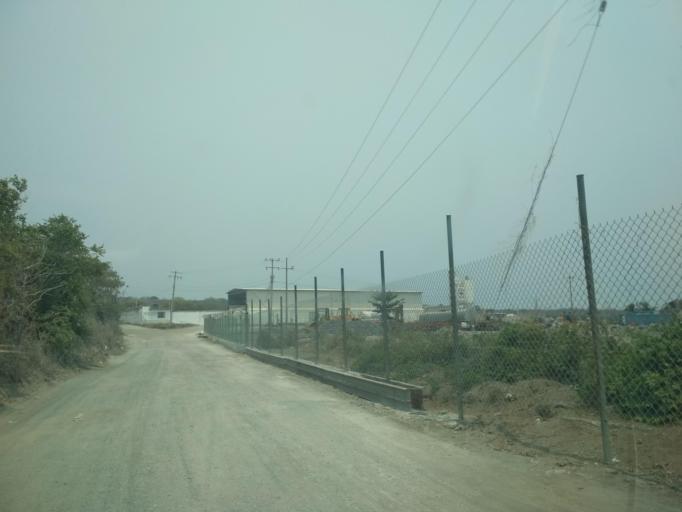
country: MX
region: Veracruz
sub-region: Veracruz
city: Delfino Victoria (Santa Fe)
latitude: 19.2259
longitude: -96.2594
